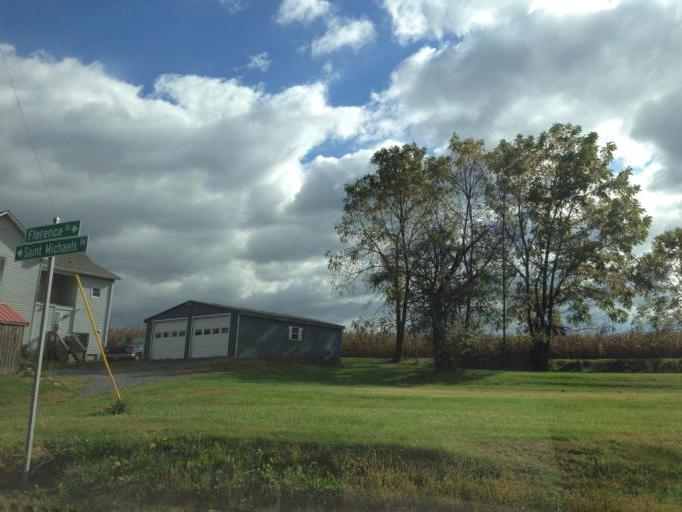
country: US
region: Maryland
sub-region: Carroll County
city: Mount Airy
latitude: 39.3221
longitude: -77.1190
